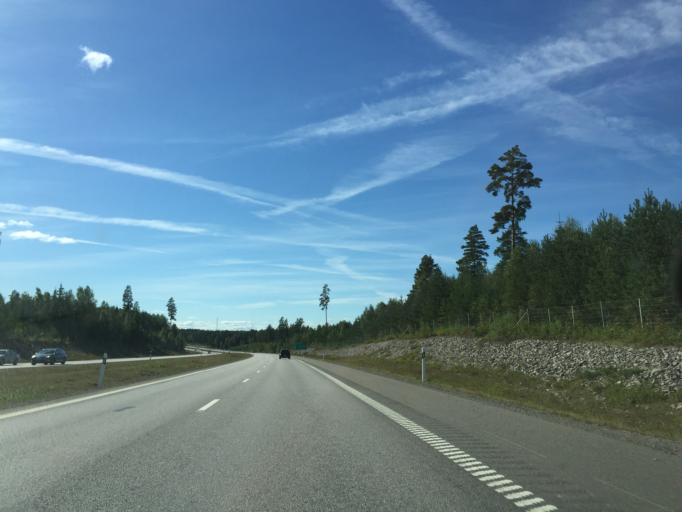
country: SE
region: OErebro
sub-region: Lindesbergs Kommun
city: Fellingsbro
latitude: 59.3755
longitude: 15.6034
